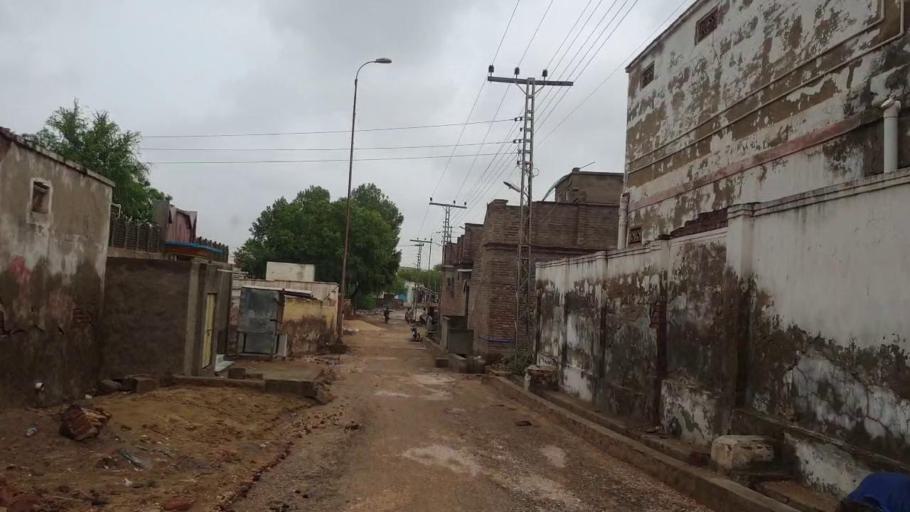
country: PK
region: Sindh
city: Diplo
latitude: 24.4638
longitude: 69.5817
